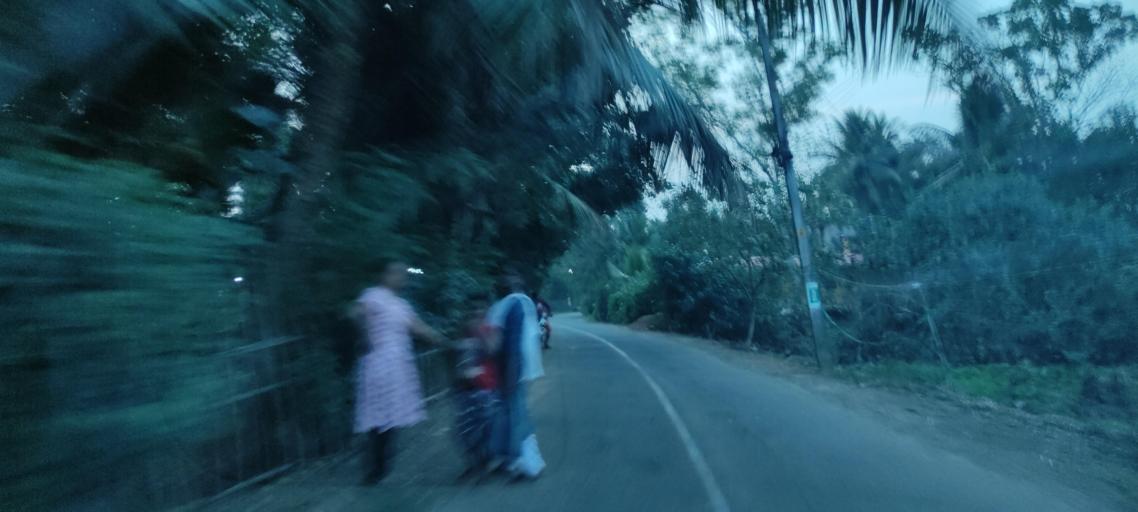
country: IN
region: Kerala
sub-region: Alappuzha
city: Mavelikara
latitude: 9.3307
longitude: 76.4927
